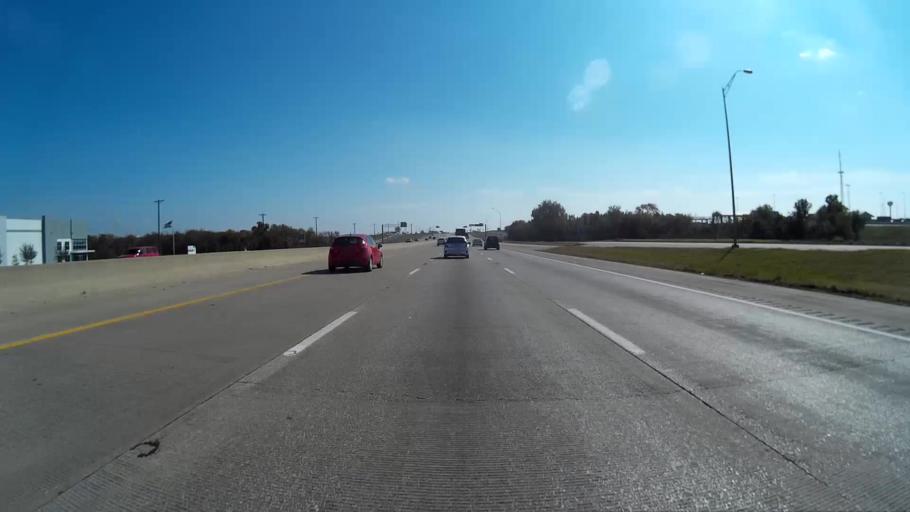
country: US
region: Texas
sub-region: Dallas County
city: Wilmer
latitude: 32.6192
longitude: -96.6930
